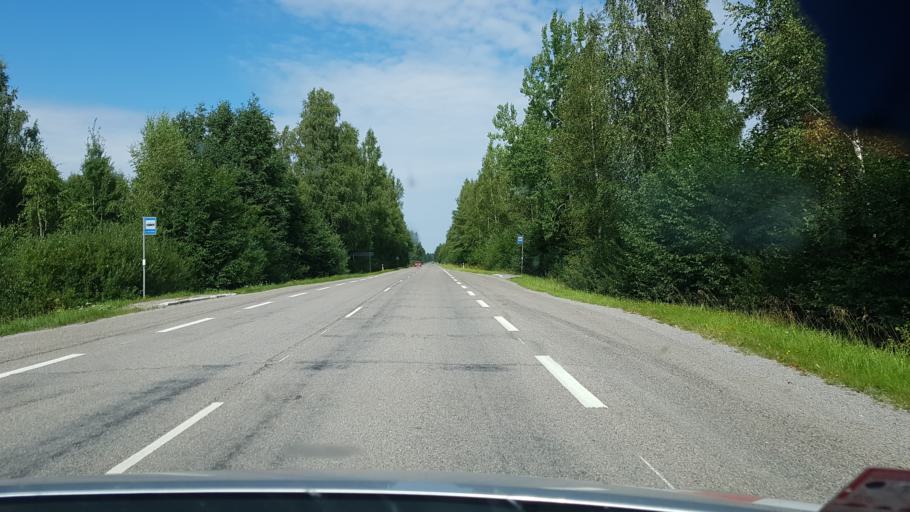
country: EE
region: Raplamaa
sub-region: Jaervakandi vald
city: Jarvakandi
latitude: 58.8033
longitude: 24.8121
